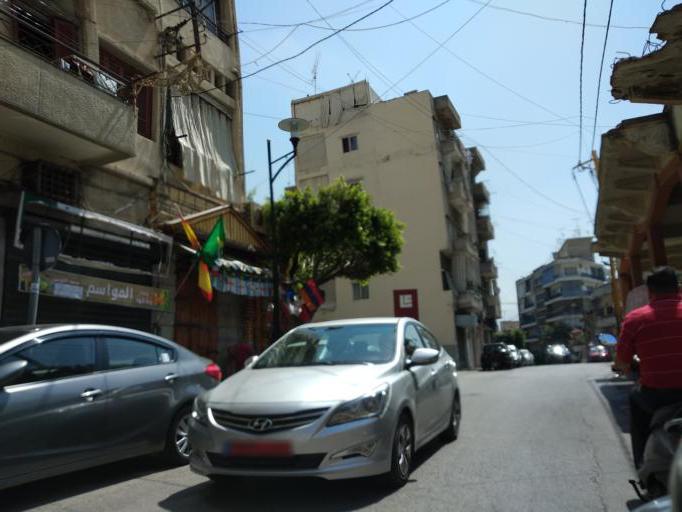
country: LB
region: Beyrouth
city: Beirut
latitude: 33.8921
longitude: 35.5295
